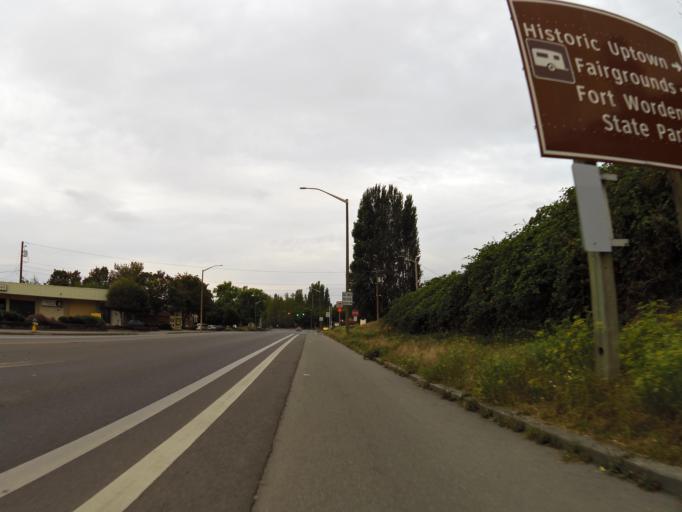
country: US
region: Washington
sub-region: Jefferson County
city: Port Townsend
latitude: 48.1101
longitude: -122.7681
